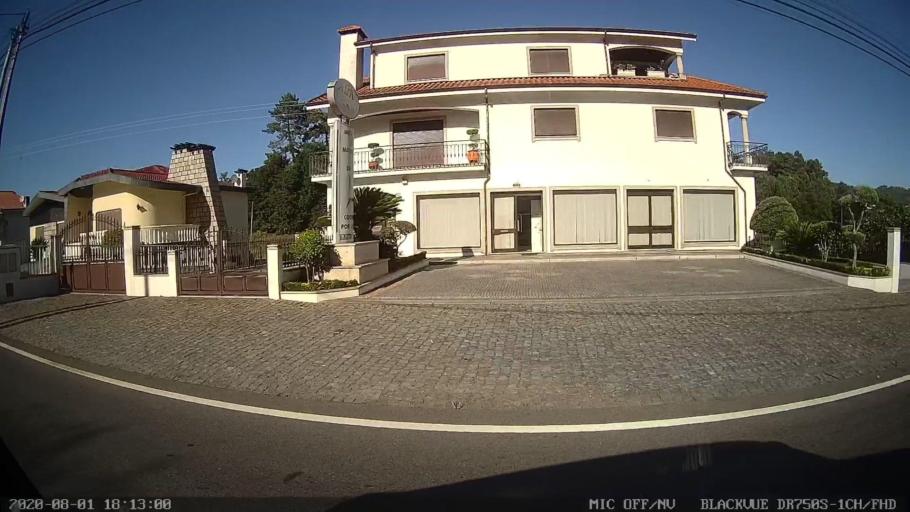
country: PT
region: Porto
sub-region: Santo Tirso
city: Sao Miguel do Couto
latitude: 41.2856
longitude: -8.4717
